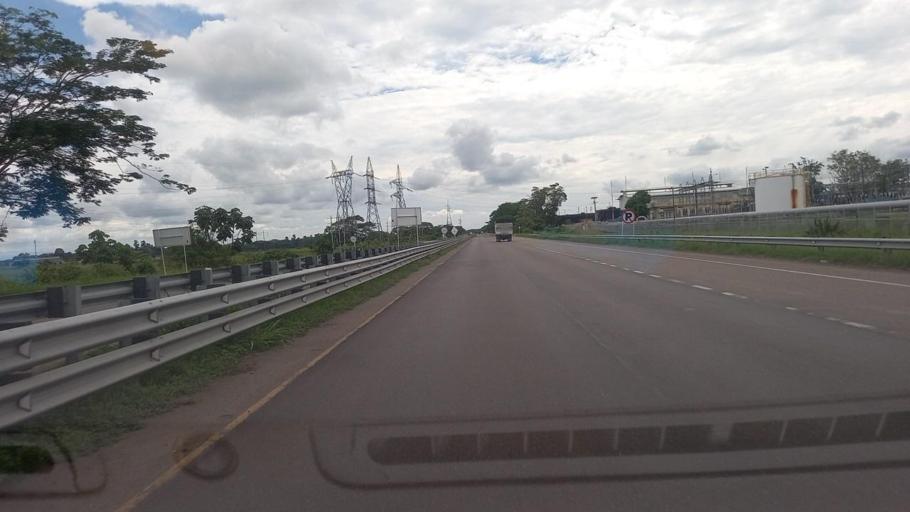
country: CO
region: Boyaca
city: Puerto Boyaca
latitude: 6.0673
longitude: -74.5565
